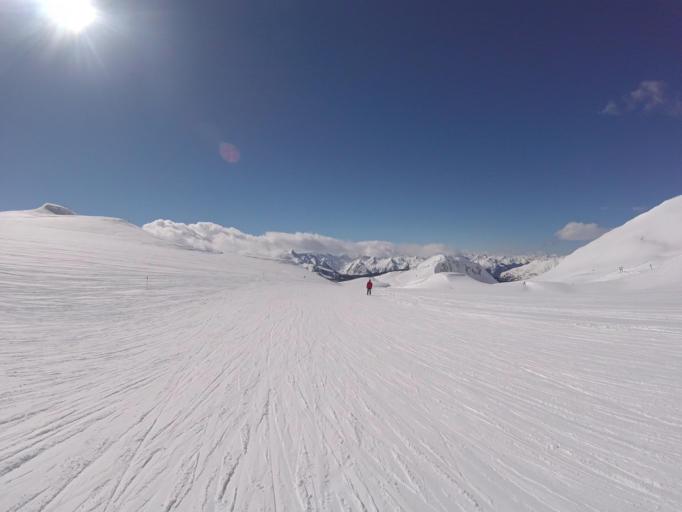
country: ES
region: Catalonia
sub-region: Provincia de Lleida
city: Espot
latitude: 42.6765
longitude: 0.9924
